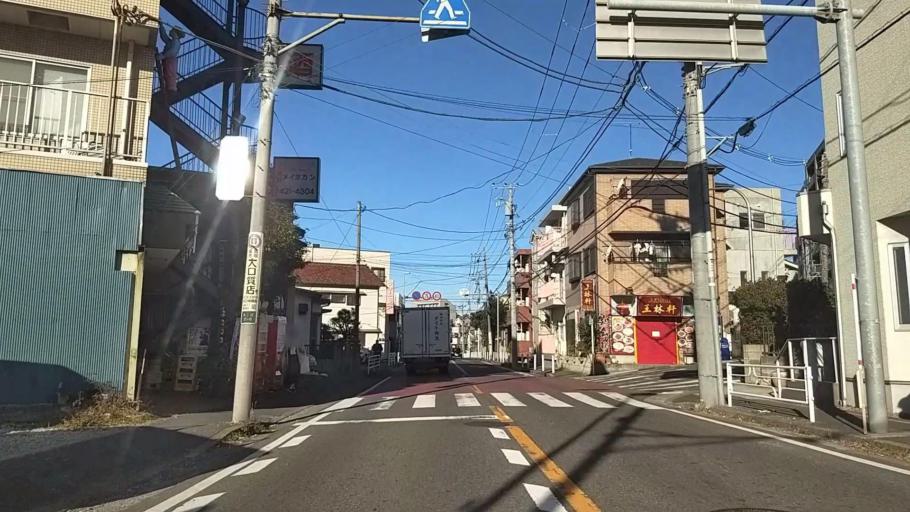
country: JP
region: Kanagawa
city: Yokohama
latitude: 35.4900
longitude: 139.6513
